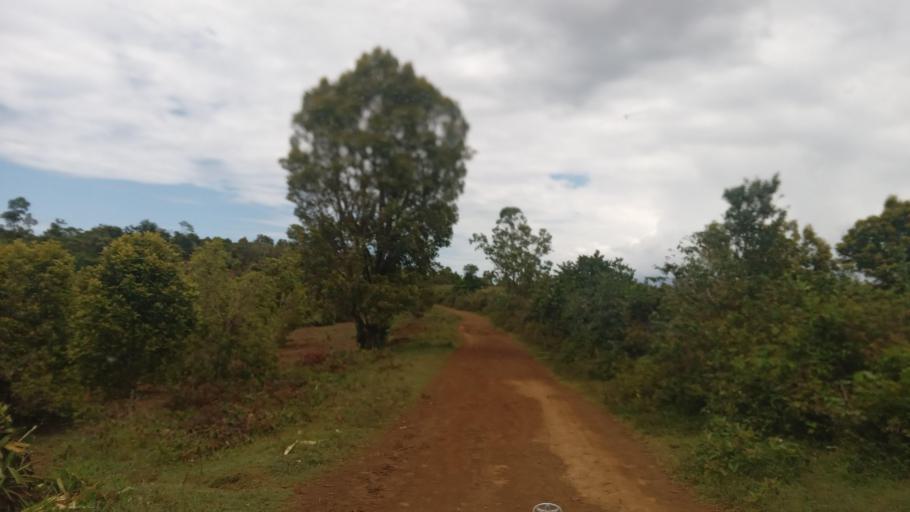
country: MG
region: Atsimo-Atsinanana
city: Vohipaho
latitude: -23.6208
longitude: 47.5794
